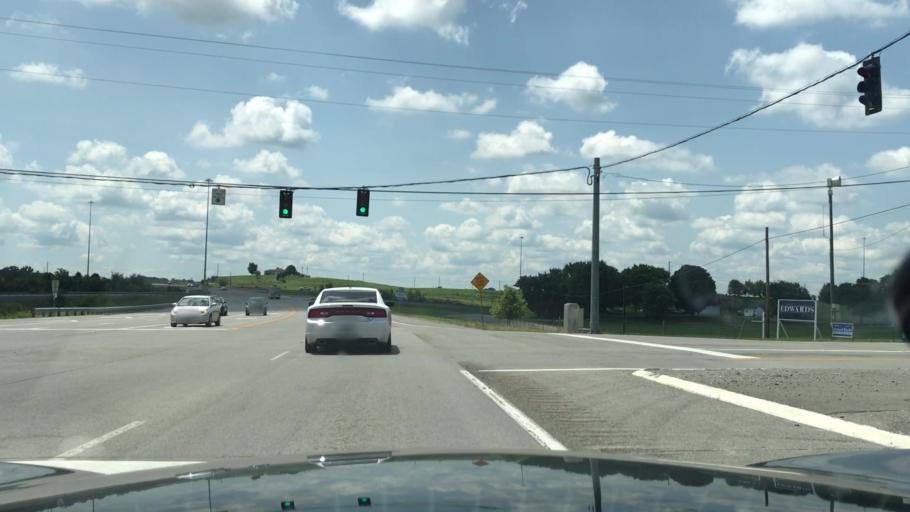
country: US
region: Kentucky
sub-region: Adair County
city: Columbia
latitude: 37.0761
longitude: -85.3383
